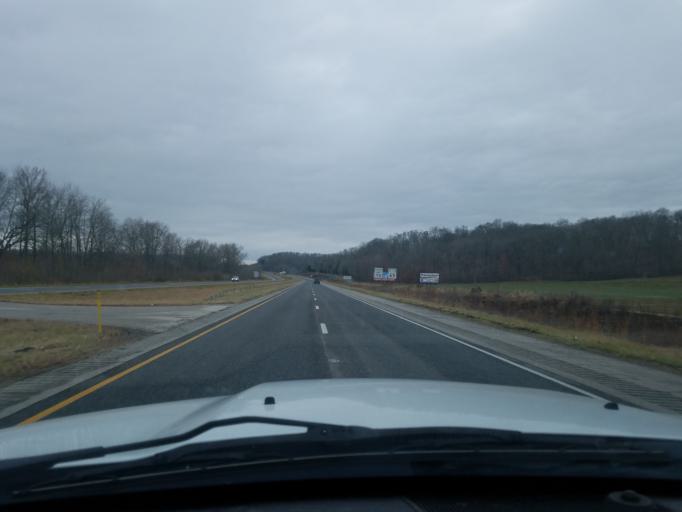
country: US
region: Indiana
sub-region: Dubois County
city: Ferdinand
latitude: 38.2222
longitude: -86.7139
